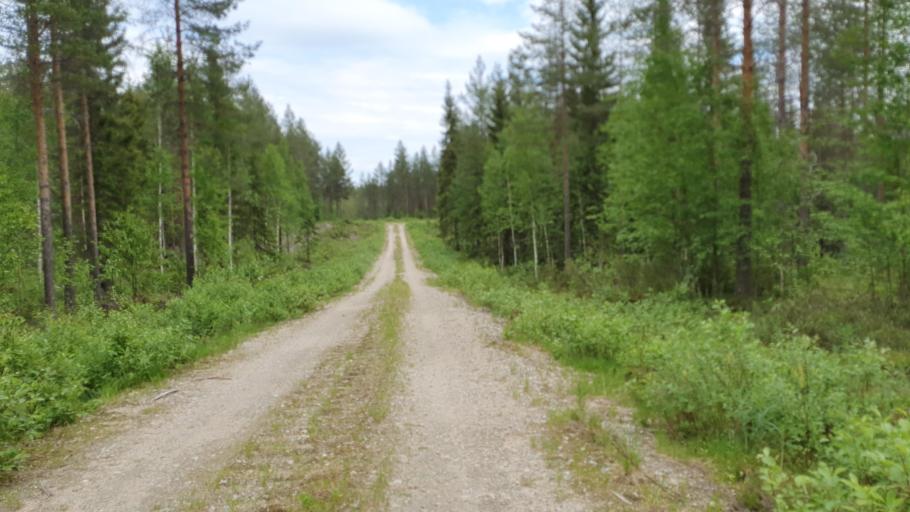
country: FI
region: Kainuu
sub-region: Kehys-Kainuu
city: Kuhmo
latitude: 64.4465
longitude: 29.7038
